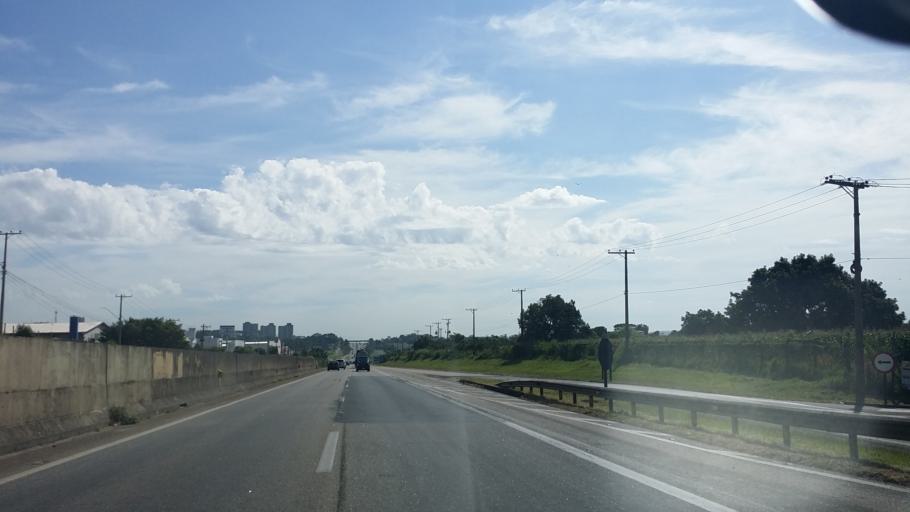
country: BR
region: Sao Paulo
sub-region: Indaiatuba
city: Indaiatuba
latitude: -23.1085
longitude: -47.2059
